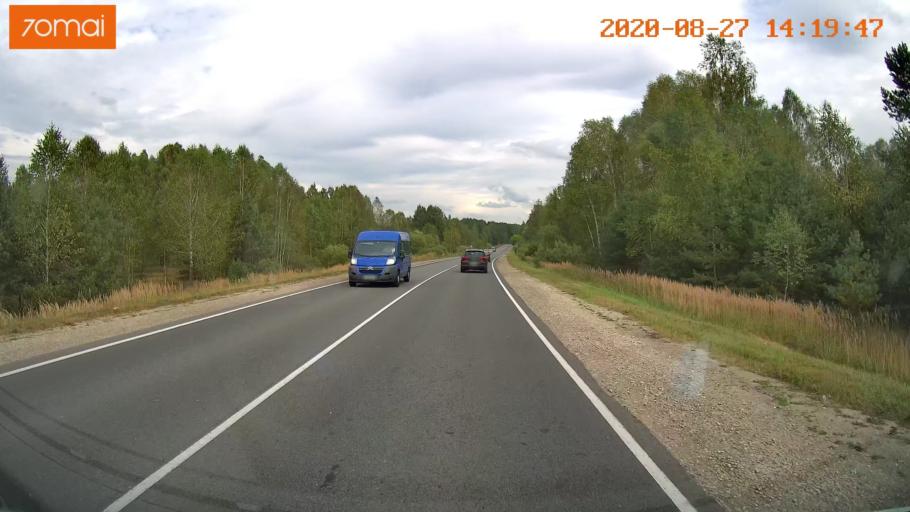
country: RU
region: Rjazan
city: Spas-Klepiki
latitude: 55.1495
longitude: 40.2608
